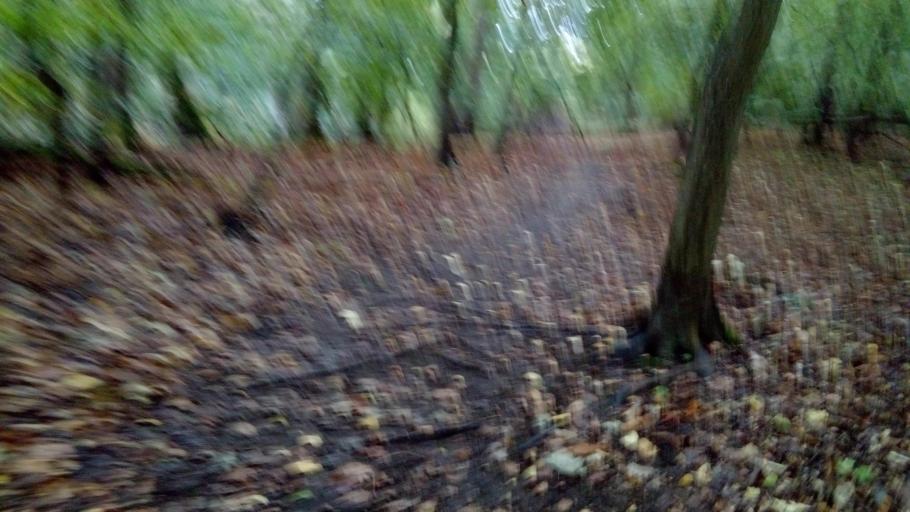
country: DE
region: North Rhine-Westphalia
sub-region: Regierungsbezirk Arnsberg
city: Bochum
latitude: 51.4464
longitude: 7.2696
